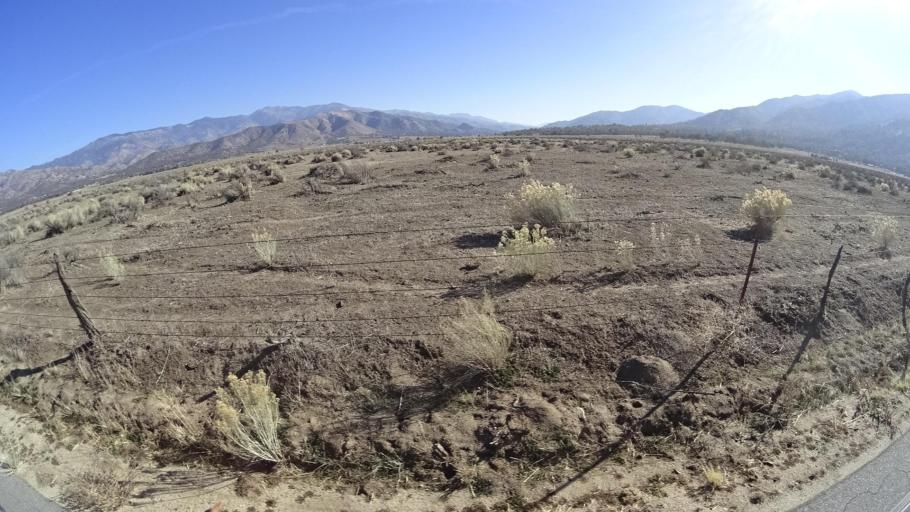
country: US
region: California
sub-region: Kern County
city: Bodfish
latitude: 35.4060
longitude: -118.5234
